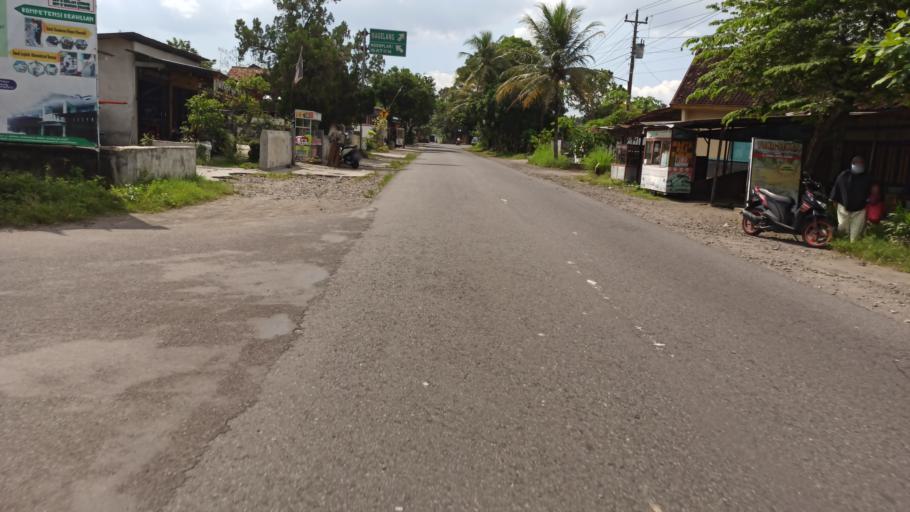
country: ID
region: Daerah Istimewa Yogyakarta
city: Sleman
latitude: -7.6826
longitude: 110.2989
